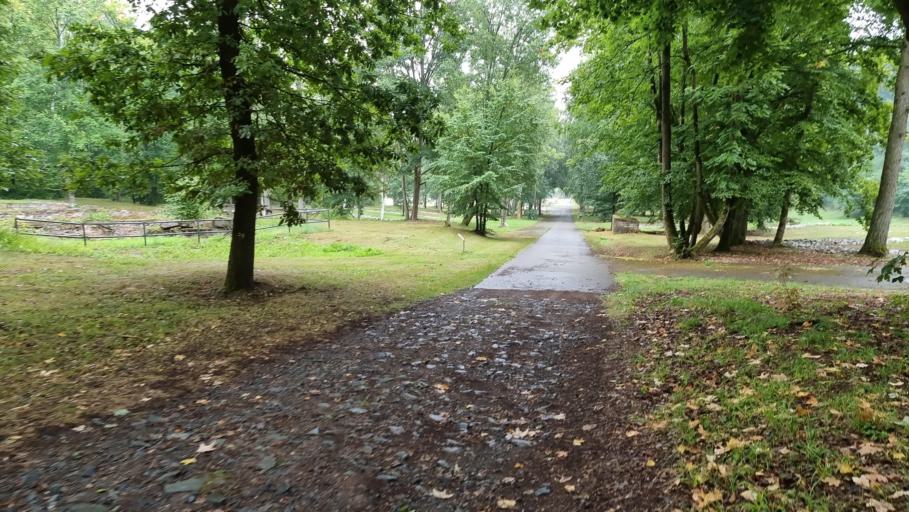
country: DE
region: Thuringia
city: Niedersachswerfen
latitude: 51.5356
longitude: 10.7438
